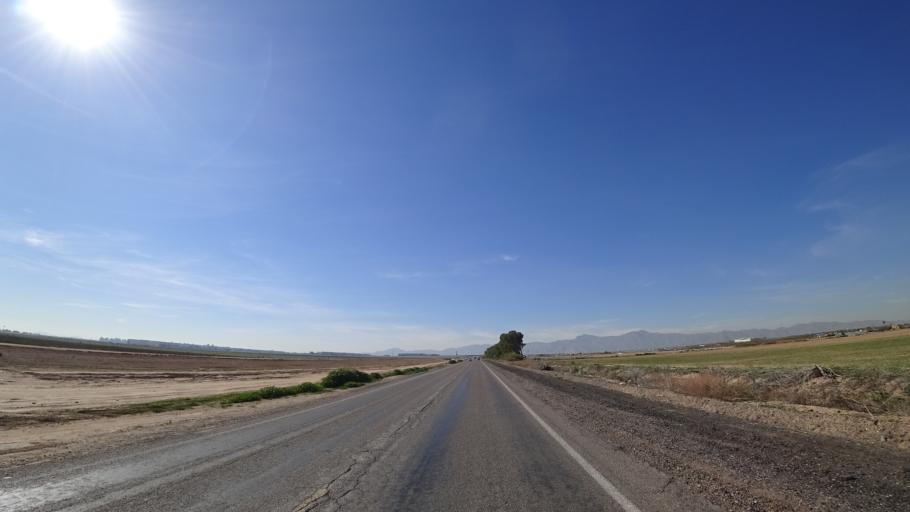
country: US
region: Arizona
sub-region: Maricopa County
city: Litchfield Park
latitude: 33.5082
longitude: -112.4035
